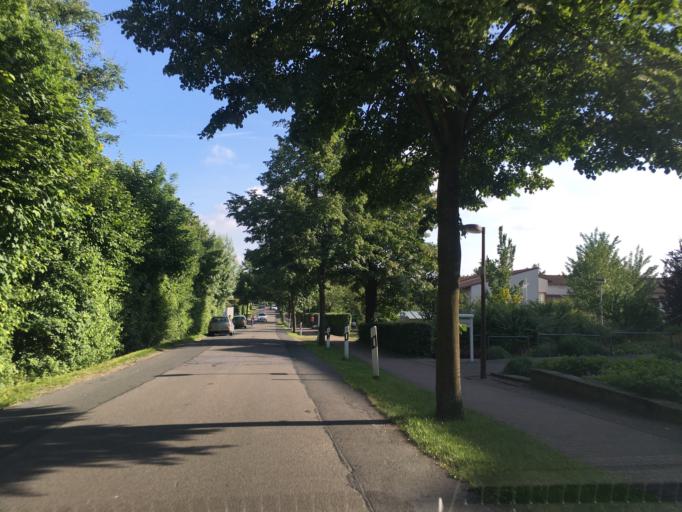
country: DE
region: North Rhine-Westphalia
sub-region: Regierungsbezirk Munster
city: Altenberge
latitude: 52.0424
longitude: 7.4638
